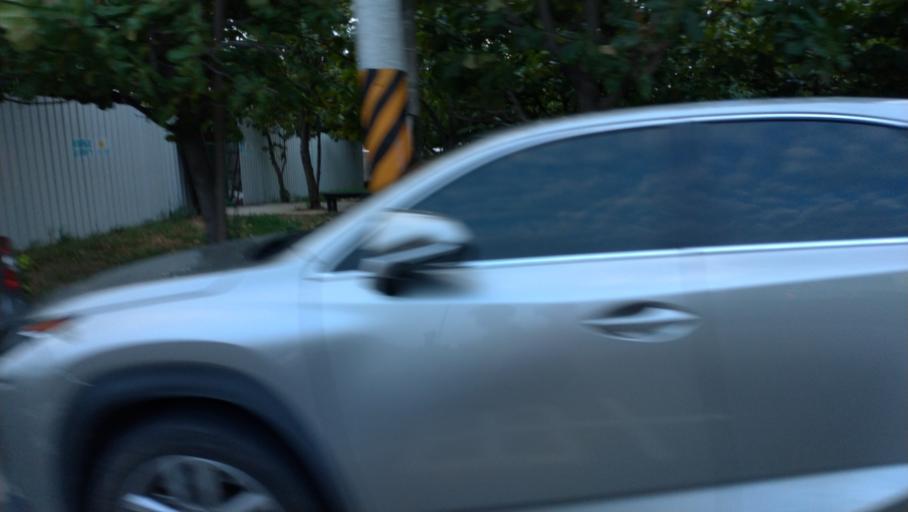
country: TW
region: Taiwan
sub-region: Hsinchu
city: Hsinchu
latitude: 24.7832
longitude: 120.9154
